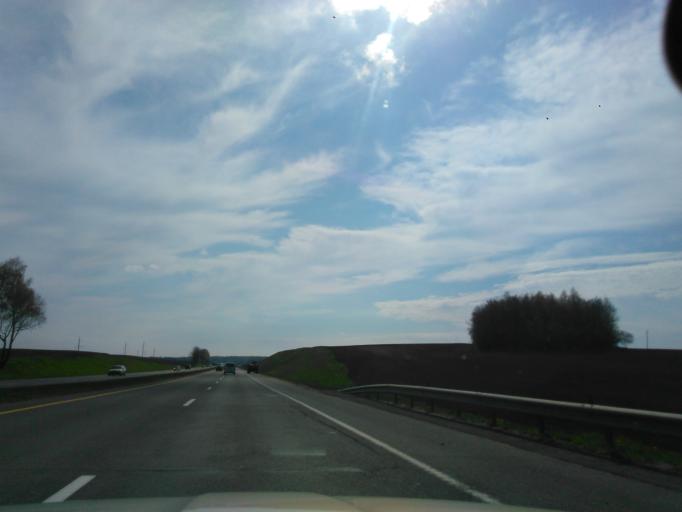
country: BY
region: Minsk
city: Novosel'ye
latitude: 53.9162
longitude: 27.2208
